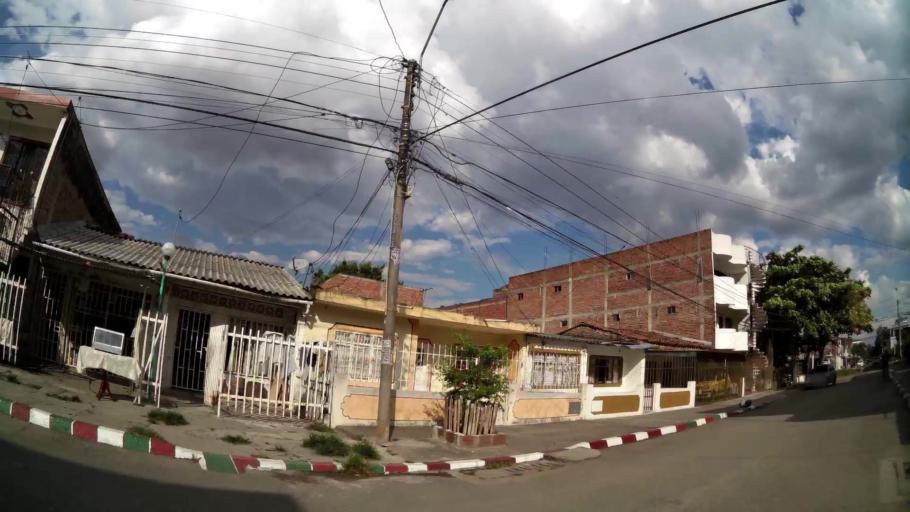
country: CO
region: Valle del Cauca
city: Cali
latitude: 3.4090
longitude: -76.5125
